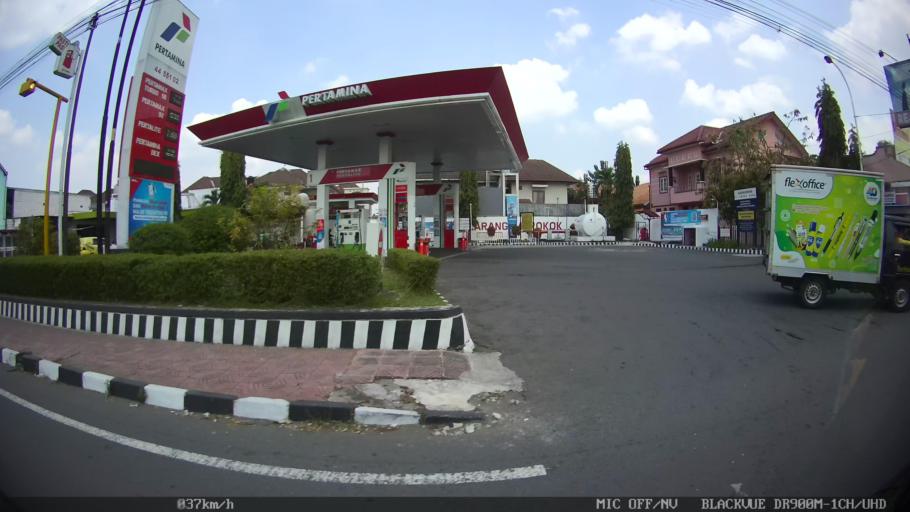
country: ID
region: Daerah Istimewa Yogyakarta
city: Yogyakarta
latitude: -7.8109
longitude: 110.4050
